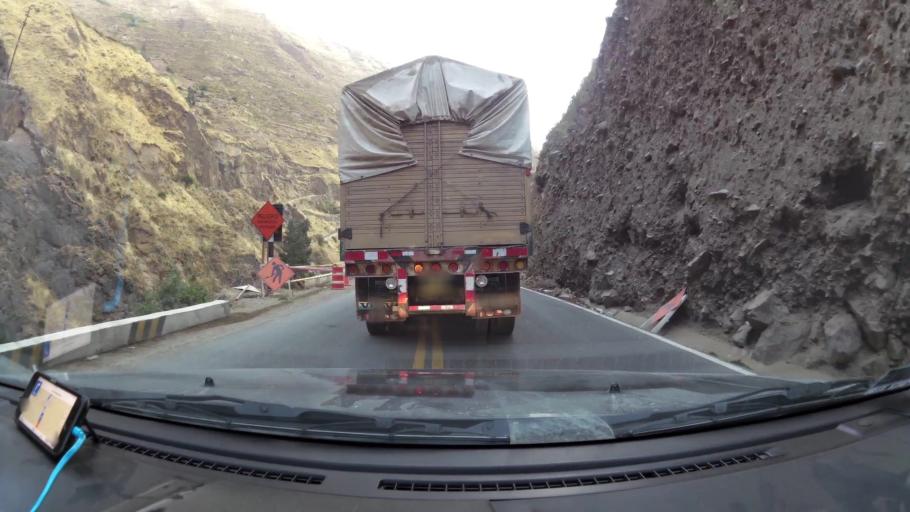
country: PE
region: Lima
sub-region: Provincia de Huarochiri
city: San Mateo
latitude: -11.8092
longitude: -76.3431
